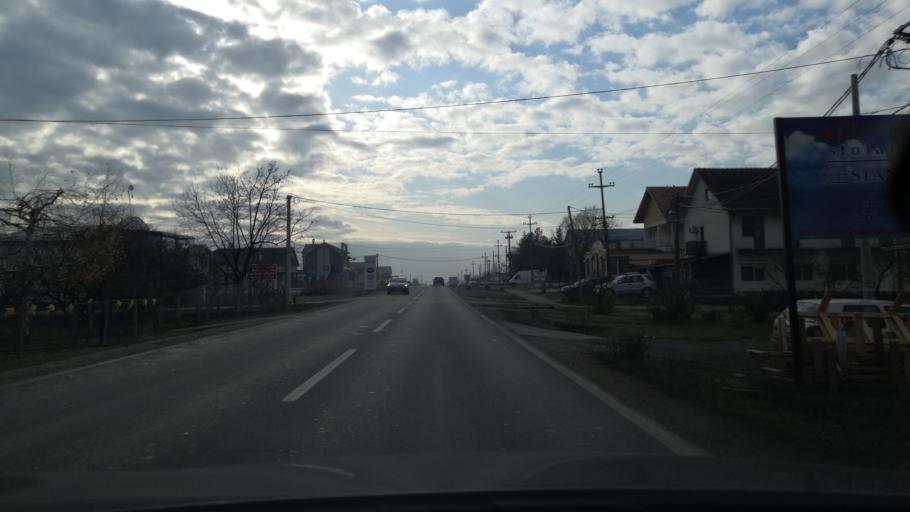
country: RS
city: Ugrinovci
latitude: 44.8684
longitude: 20.2042
